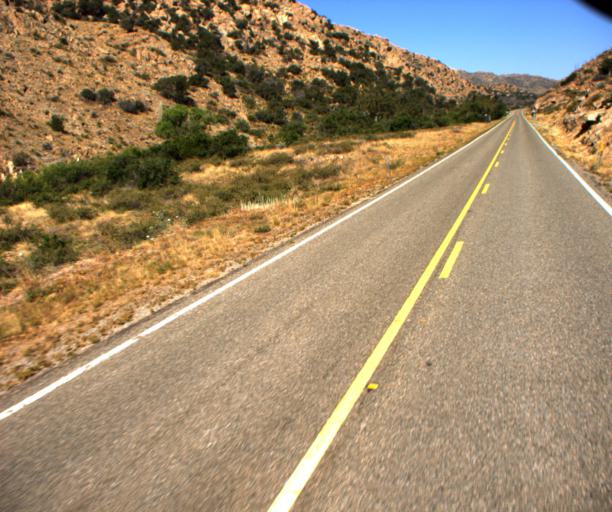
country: US
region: Arizona
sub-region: Graham County
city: Swift Trail Junction
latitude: 32.5622
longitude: -109.7927
